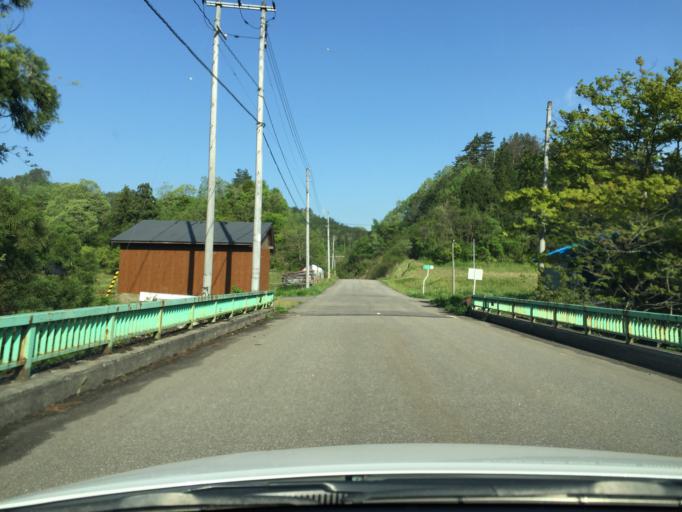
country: JP
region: Fukushima
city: Kitakata
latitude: 37.6739
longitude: 139.6426
